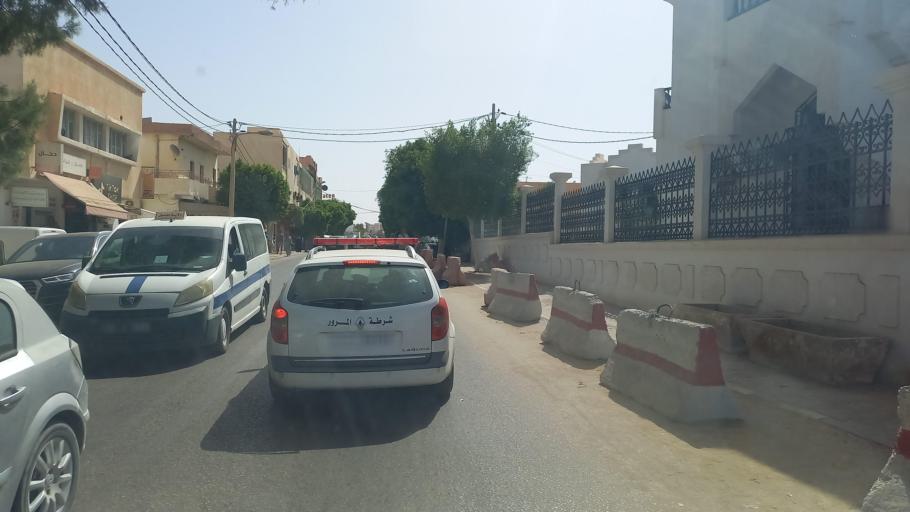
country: TN
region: Madanin
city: Medenine
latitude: 33.3430
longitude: 10.4917
